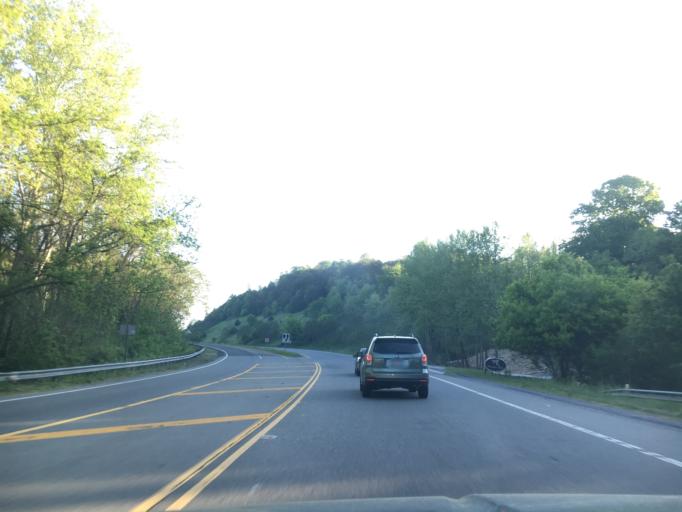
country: US
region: Virginia
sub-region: Campbell County
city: Rustburg
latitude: 37.3037
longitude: -79.1090
